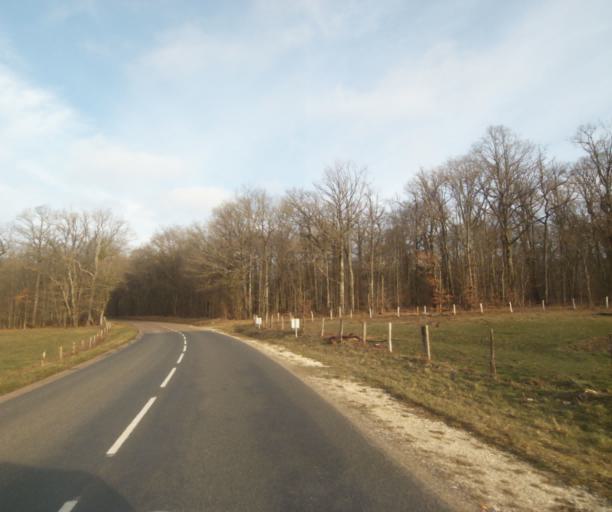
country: FR
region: Champagne-Ardenne
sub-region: Departement de la Marne
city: Sermaize-les-Bains
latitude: 48.7492
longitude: 4.9043
